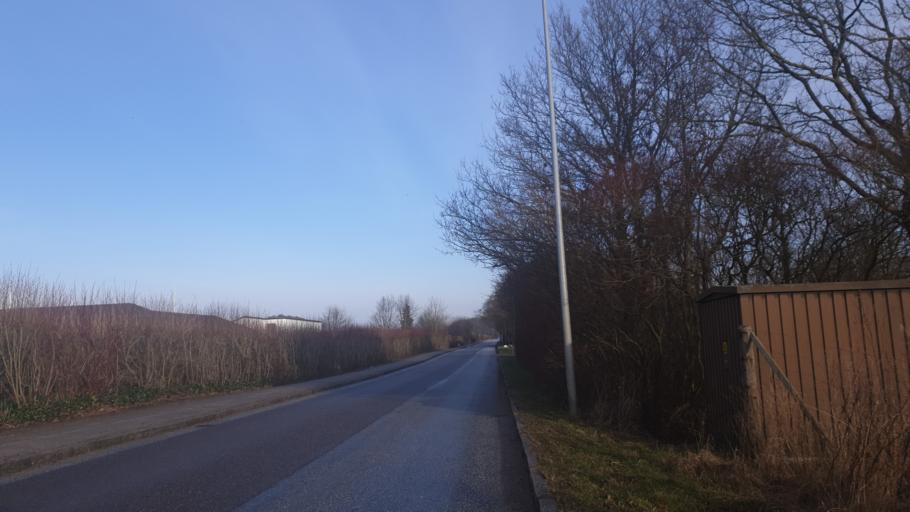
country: DK
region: Central Jutland
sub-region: Hedensted Kommune
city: Hedensted
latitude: 55.7673
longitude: 9.7212
